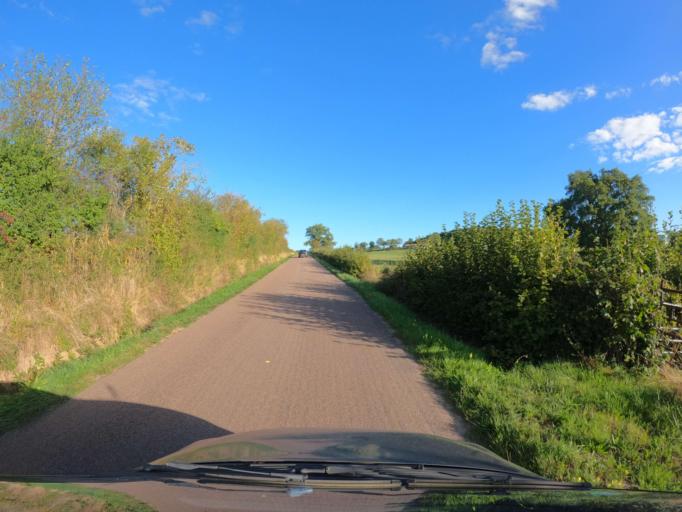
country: FR
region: Bourgogne
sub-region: Departement de Saone-et-Loire
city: Ecuisses
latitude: 46.7409
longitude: 4.5462
